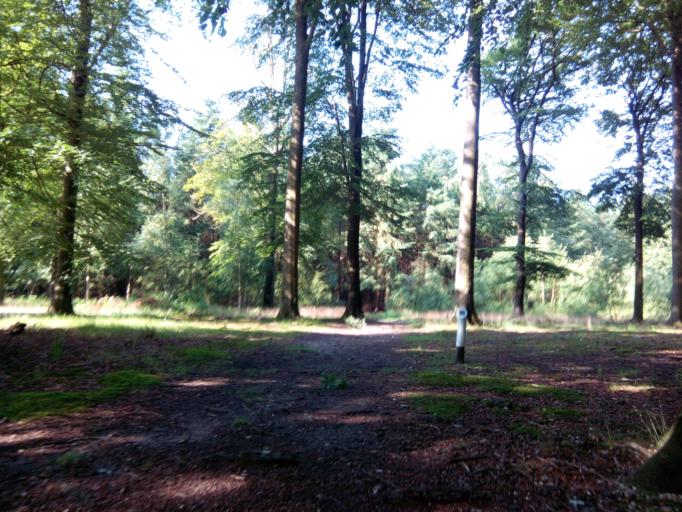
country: NL
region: Utrecht
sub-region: Gemeente Utrechtse Heuvelrug
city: Maarn
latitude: 52.0919
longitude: 5.3601
